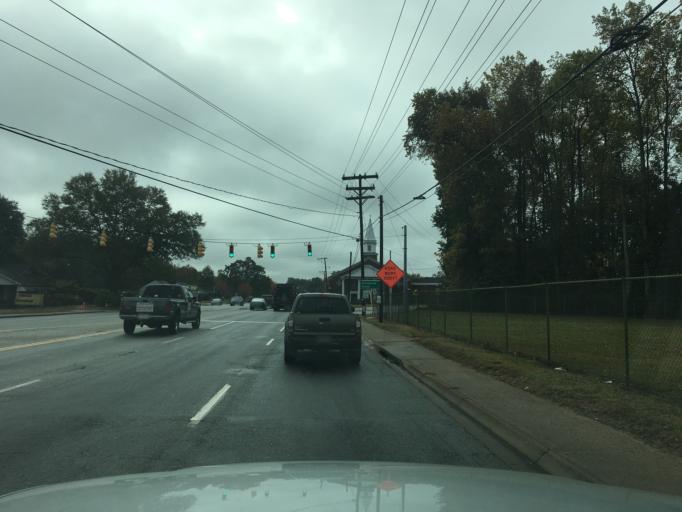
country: US
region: South Carolina
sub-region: Greenville County
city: Welcome
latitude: 34.8300
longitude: -82.4466
